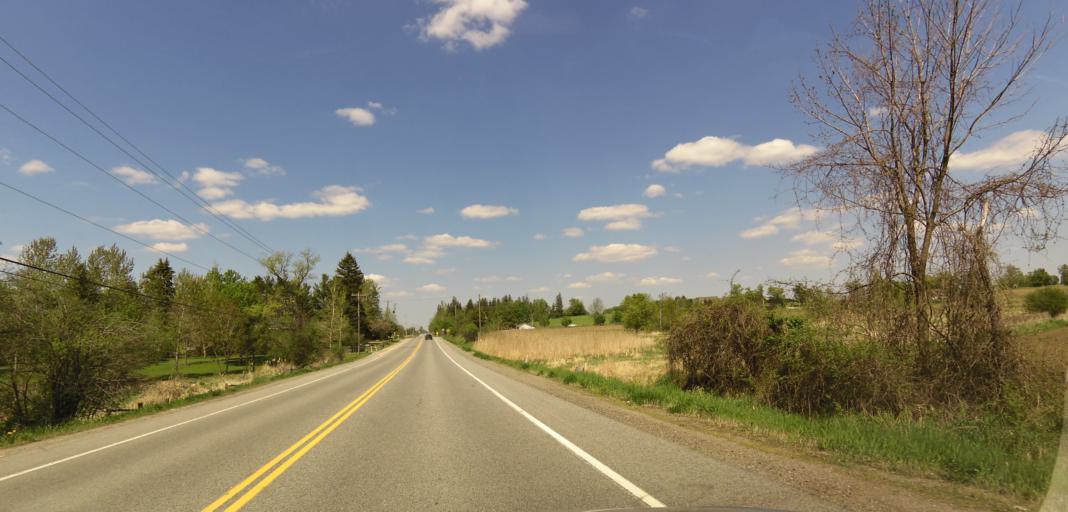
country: CA
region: Ontario
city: Brampton
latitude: 43.8366
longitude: -79.8756
